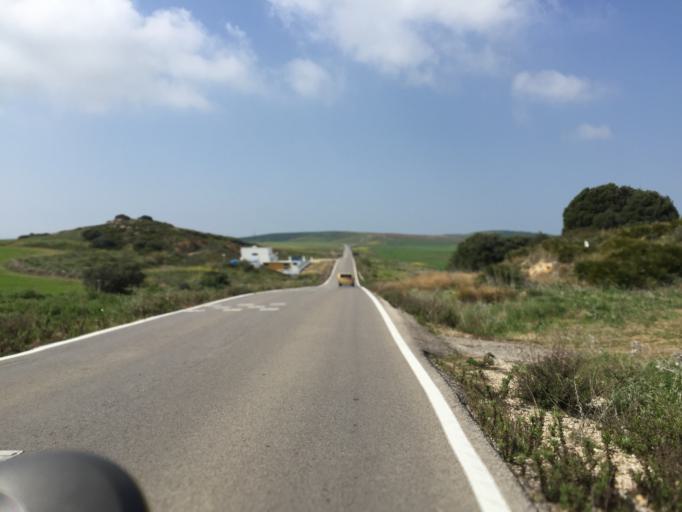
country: ES
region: Andalusia
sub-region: Provincia de Cadiz
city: Vejer de la Frontera
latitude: 36.2366
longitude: -6.0161
